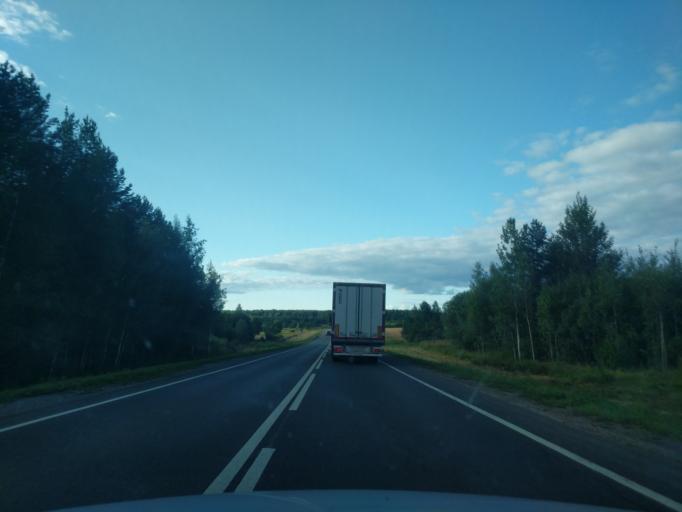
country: RU
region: Kostroma
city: Manturovo
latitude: 58.3050
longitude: 44.7270
